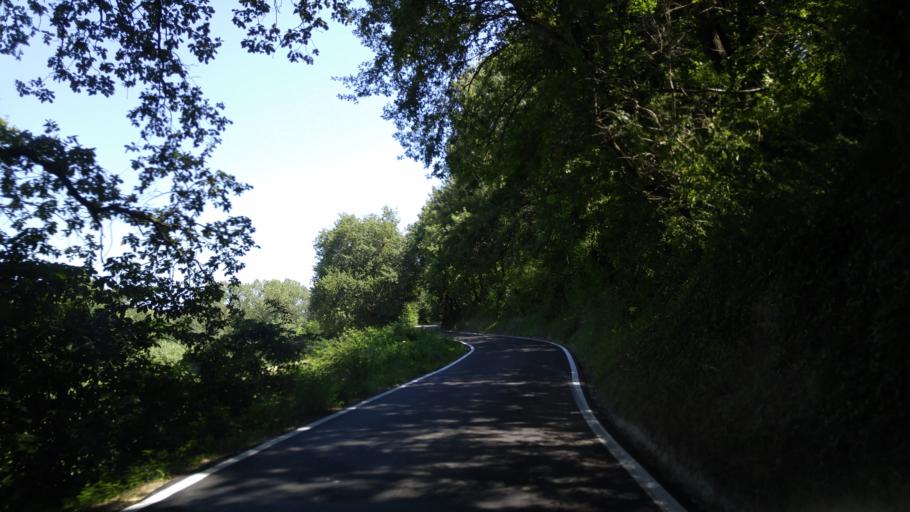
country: IT
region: The Marches
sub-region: Provincia di Pesaro e Urbino
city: Fenile
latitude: 43.8310
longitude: 12.9566
